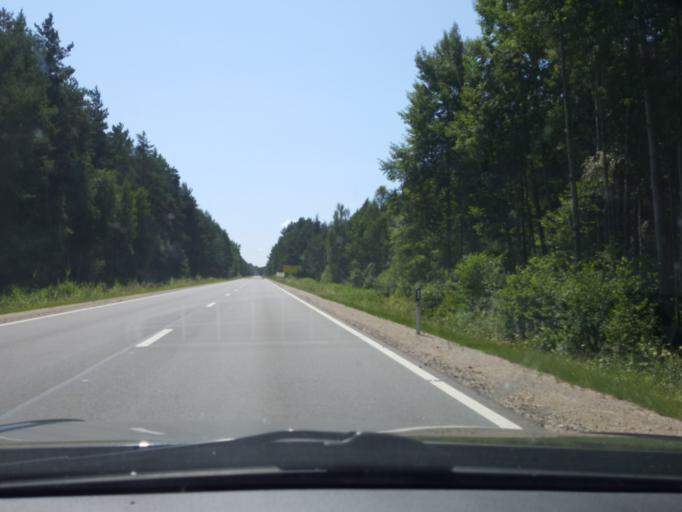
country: LV
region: Rucavas
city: Rucava
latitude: 56.1538
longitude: 21.1482
